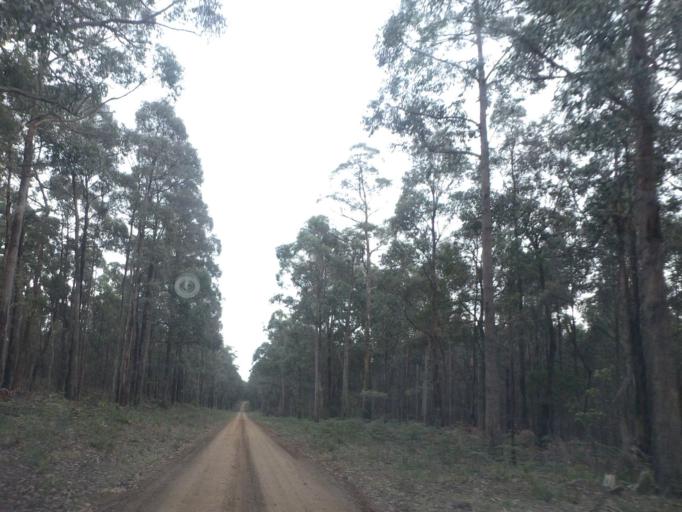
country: AU
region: Victoria
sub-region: Moorabool
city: Bacchus Marsh
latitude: -37.4256
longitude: 144.3110
